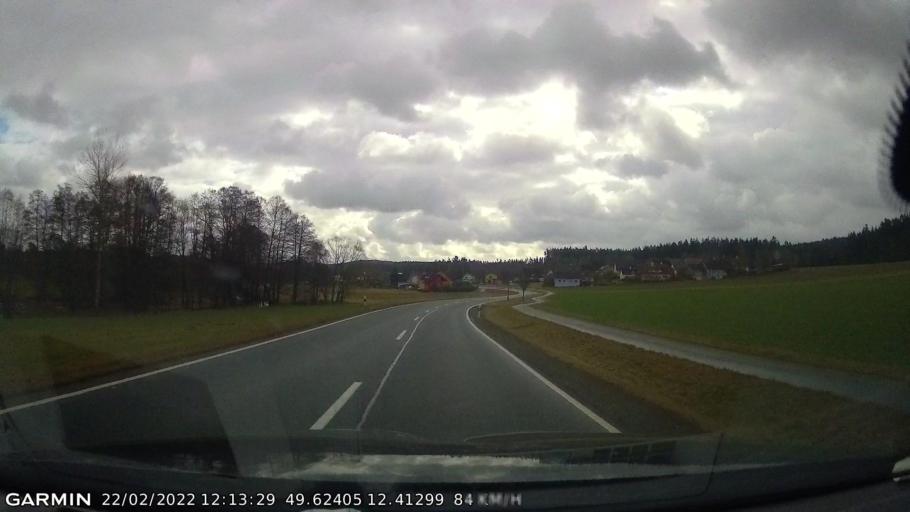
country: DE
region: Bavaria
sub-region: Upper Palatinate
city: Pleystein
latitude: 49.6238
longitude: 12.4131
